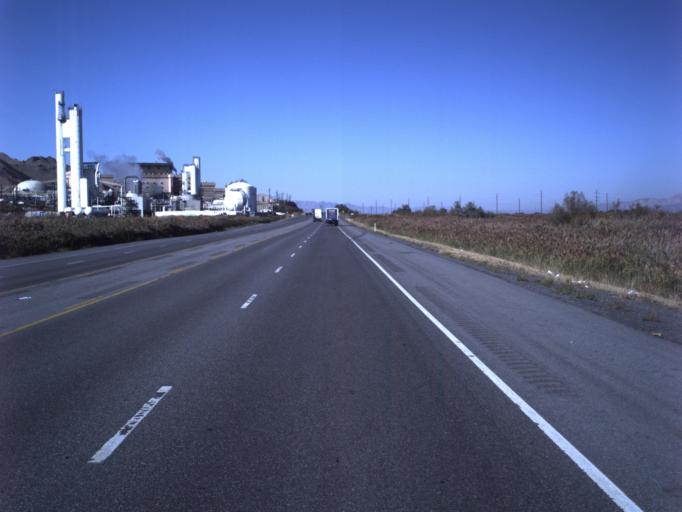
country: US
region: Utah
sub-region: Salt Lake County
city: Magna
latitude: 40.7279
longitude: -112.1801
